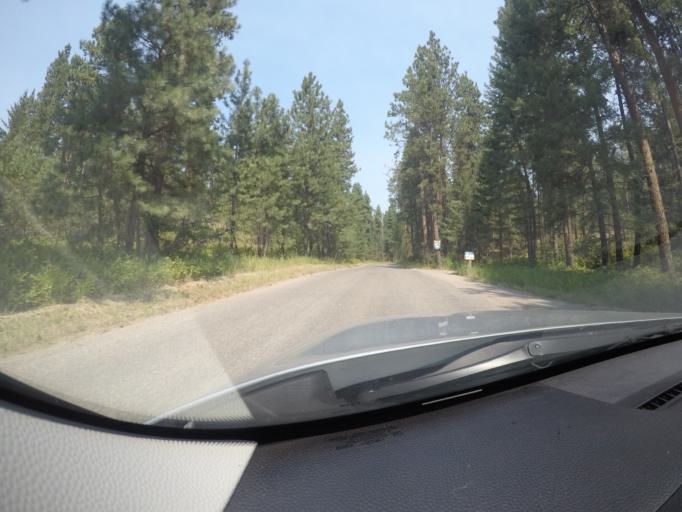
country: US
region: Montana
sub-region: Lake County
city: Polson
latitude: 47.7652
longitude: -114.1563
